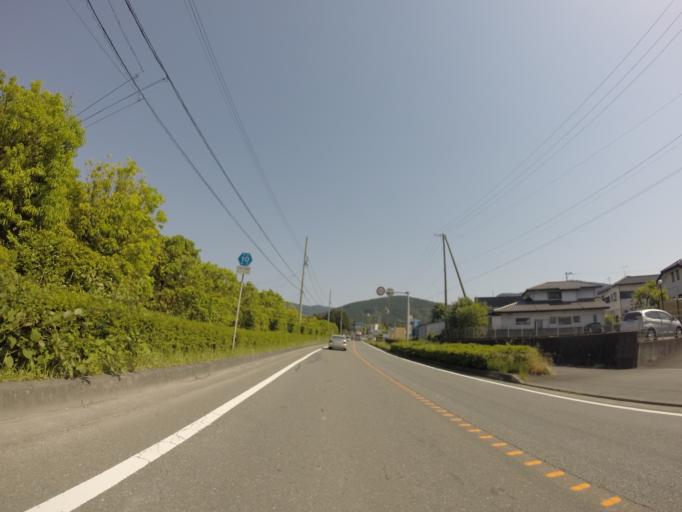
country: JP
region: Shizuoka
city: Fujinomiya
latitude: 35.1919
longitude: 138.5899
